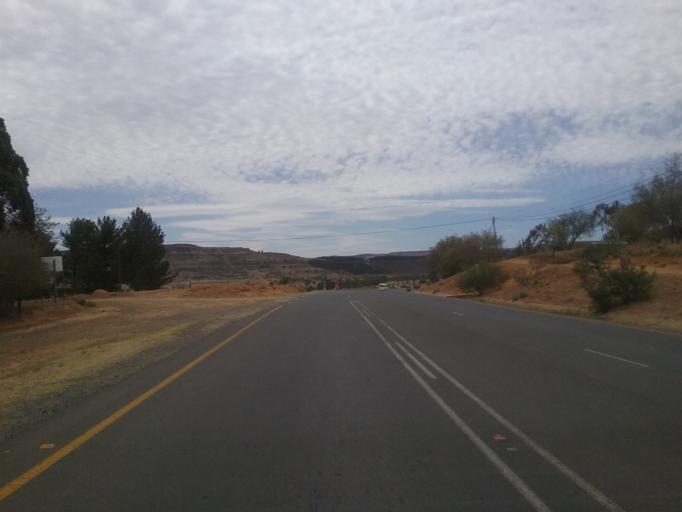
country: LS
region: Maseru
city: Nako
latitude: -29.6270
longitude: 27.4877
